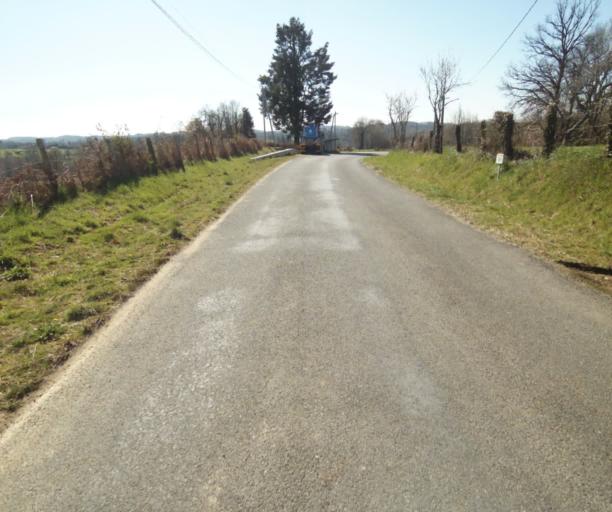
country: FR
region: Limousin
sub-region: Departement de la Correze
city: Saint-Mexant
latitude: 45.3147
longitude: 1.6465
